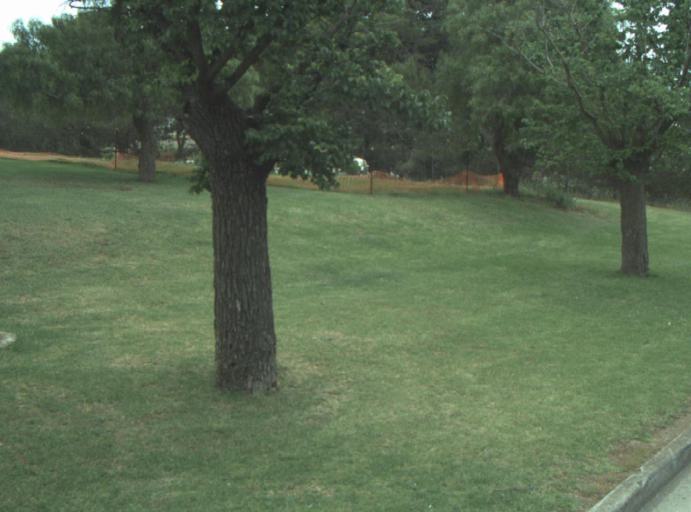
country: AU
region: Victoria
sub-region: Greater Geelong
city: Clifton Springs
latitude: -38.1144
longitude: 144.6515
